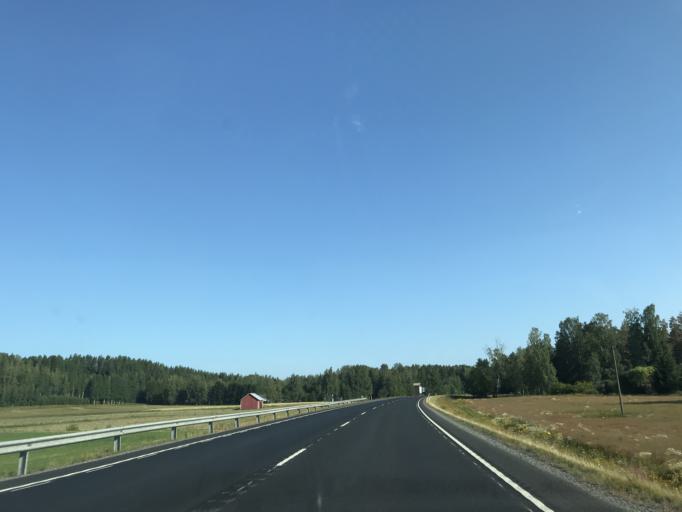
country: FI
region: Paijanne Tavastia
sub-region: Lahti
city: Lahti
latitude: 61.0989
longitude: 25.6429
